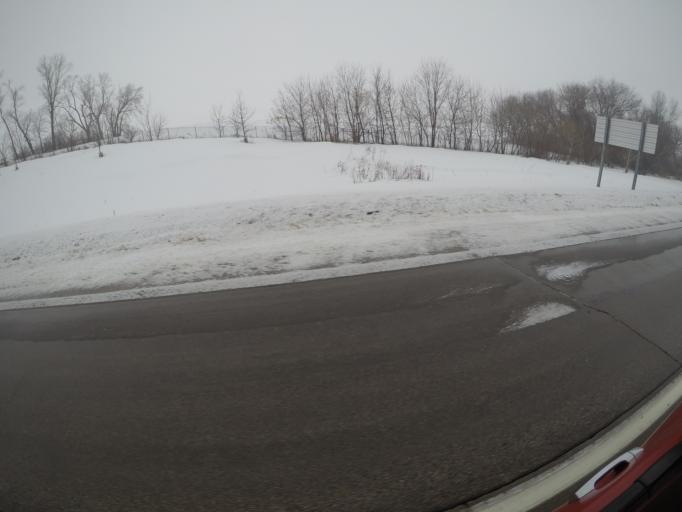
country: US
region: Minnesota
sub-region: Olmsted County
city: Oronoco
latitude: 44.1162
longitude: -92.5186
